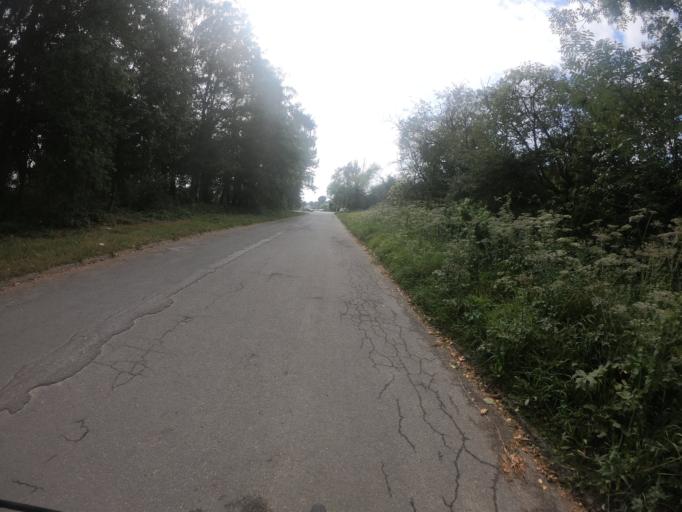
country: BE
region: Flanders
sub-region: Provincie Vlaams-Brabant
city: Wezembeek-Oppem
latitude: 50.8451
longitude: 4.5124
